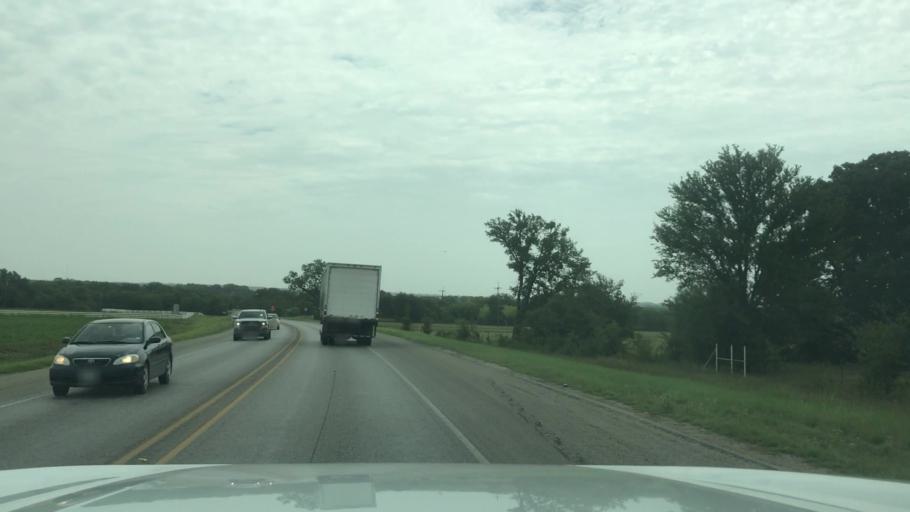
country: US
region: Texas
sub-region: Comanche County
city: De Leon
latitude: 32.1049
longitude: -98.4876
